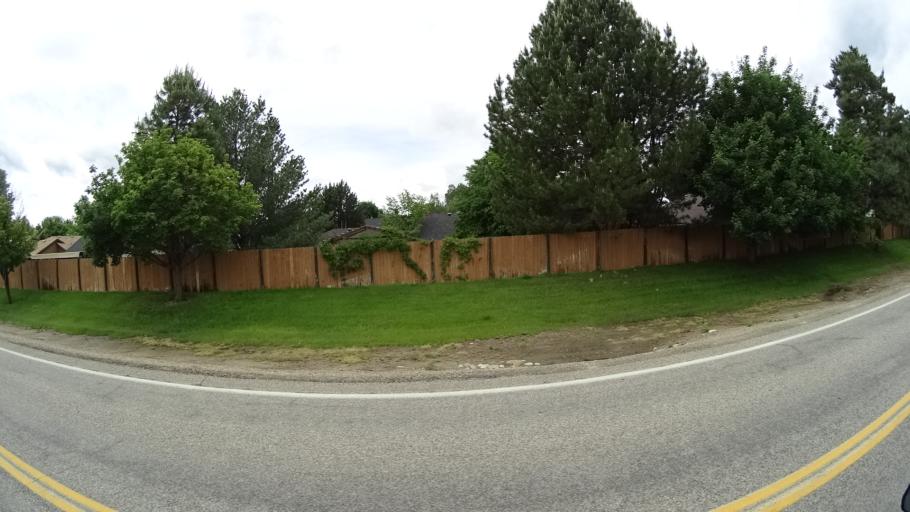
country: US
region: Idaho
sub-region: Ada County
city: Eagle
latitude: 43.7086
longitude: -116.3142
